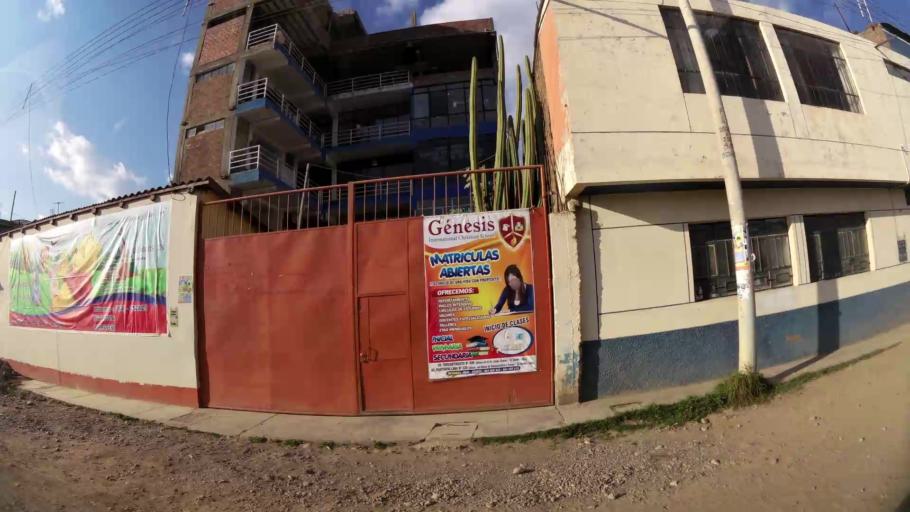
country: PE
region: Junin
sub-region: Provincia de Huancayo
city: El Tambo
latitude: -12.0506
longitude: -75.2187
